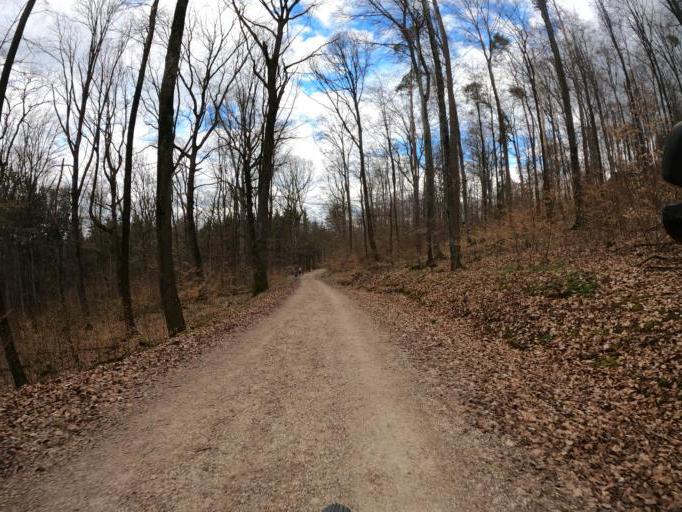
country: DE
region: Baden-Wuerttemberg
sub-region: Tuebingen Region
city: Gomaringen
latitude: 48.4685
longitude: 9.1412
